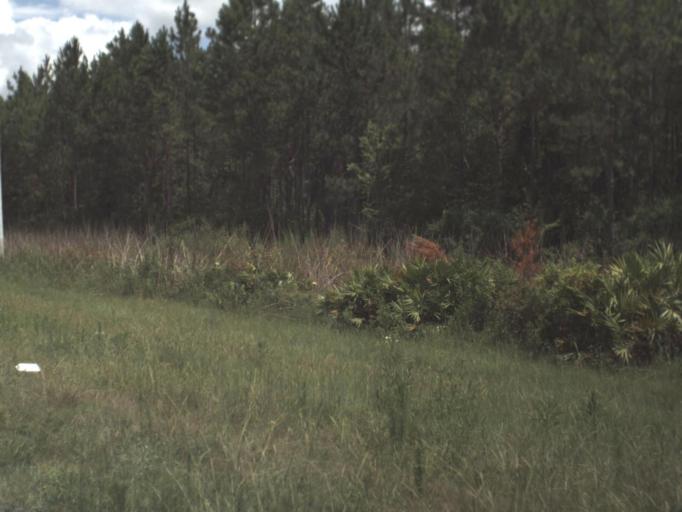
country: US
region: Florida
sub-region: Union County
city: Lake Butler
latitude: 29.9205
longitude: -82.4064
